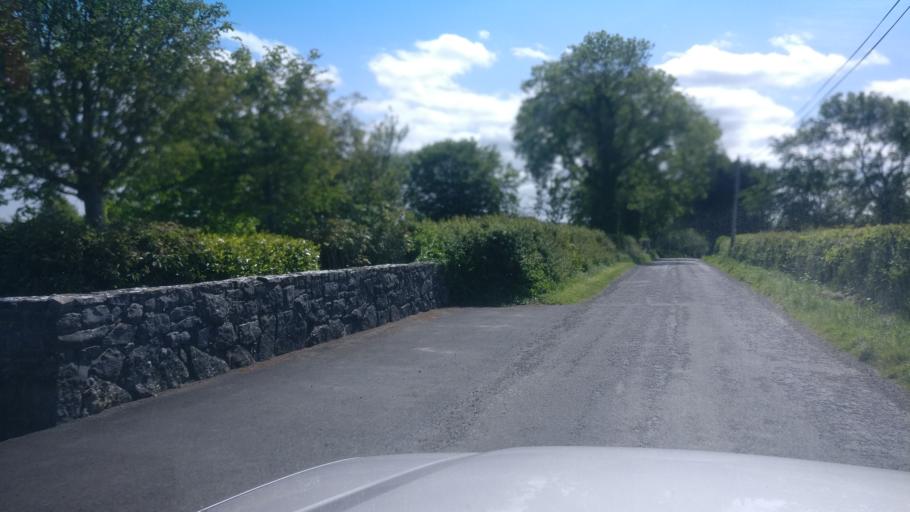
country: IE
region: Connaught
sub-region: County Galway
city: Gort
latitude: 53.1479
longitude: -8.7431
